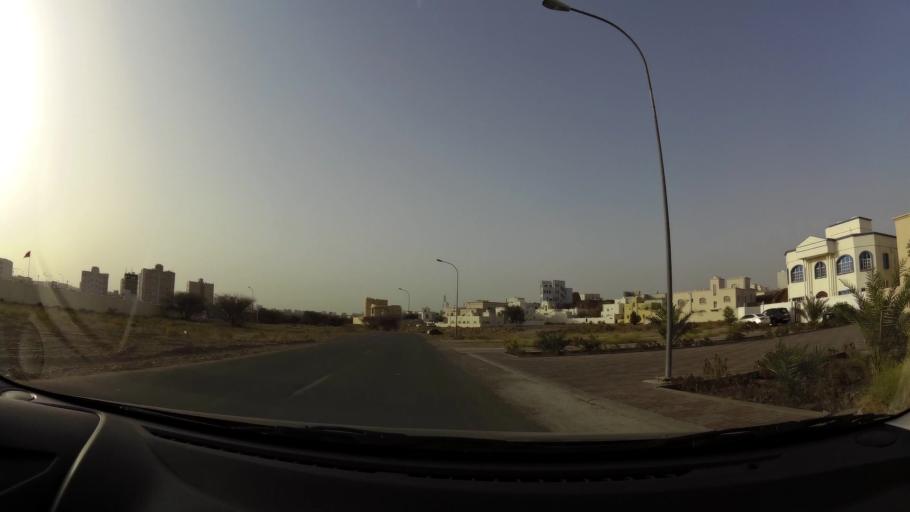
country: OM
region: Muhafazat Masqat
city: Bawshar
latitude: 23.5342
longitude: 58.3530
